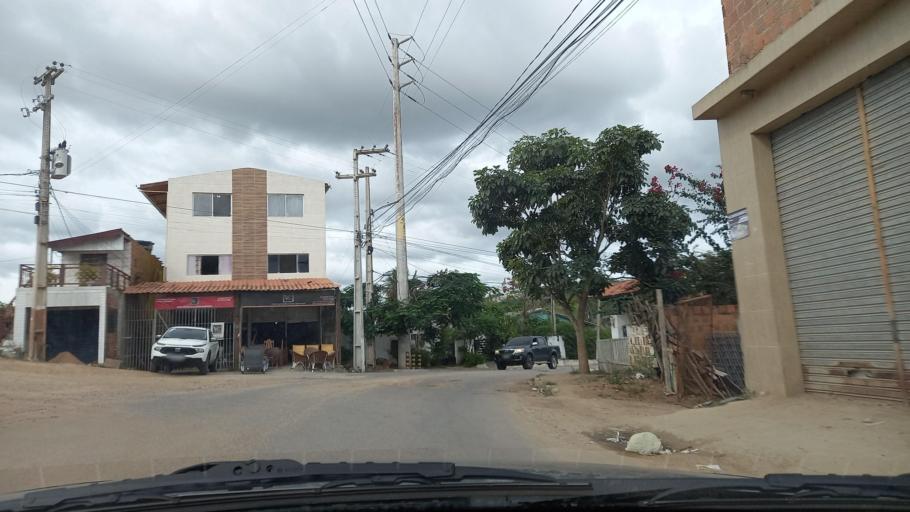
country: BR
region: Pernambuco
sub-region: Gravata
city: Gravata
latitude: -8.2055
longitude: -35.5593
